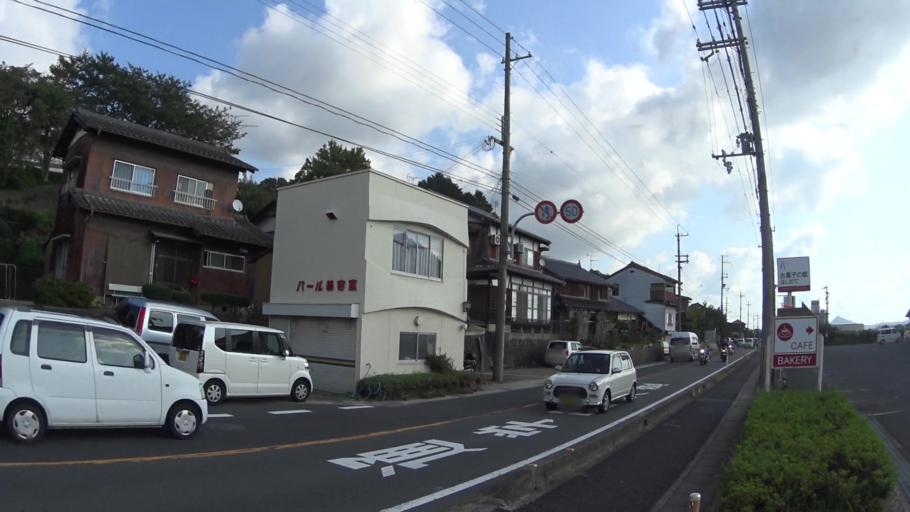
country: JP
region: Kyoto
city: Miyazu
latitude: 35.5739
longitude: 135.1703
